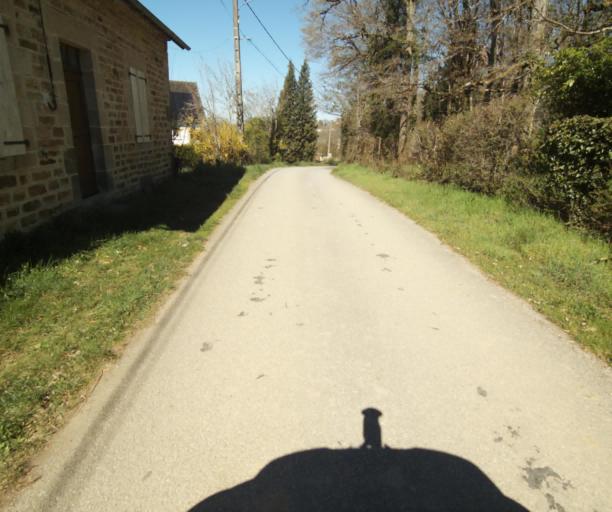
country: FR
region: Limousin
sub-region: Departement de la Correze
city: Chamboulive
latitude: 45.4278
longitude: 1.7210
